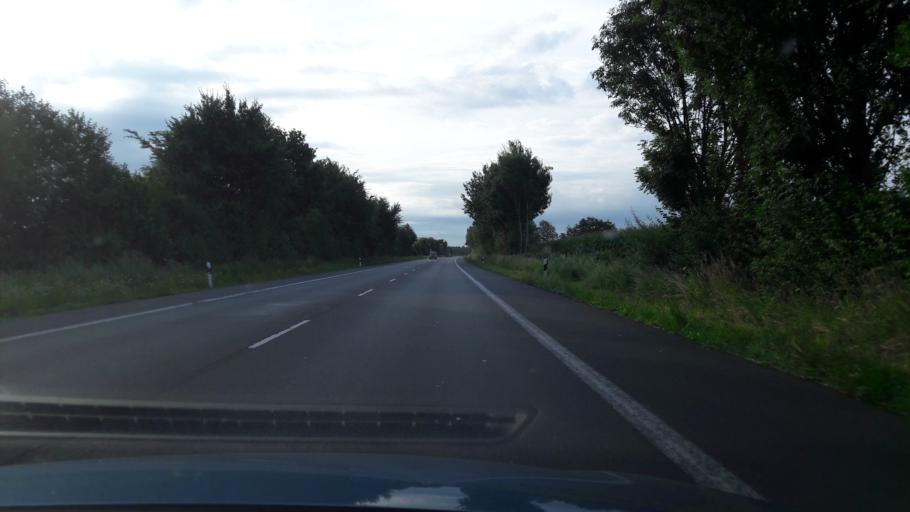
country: DE
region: North Rhine-Westphalia
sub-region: Regierungsbezirk Munster
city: Telgte
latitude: 51.9330
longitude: 7.7437
